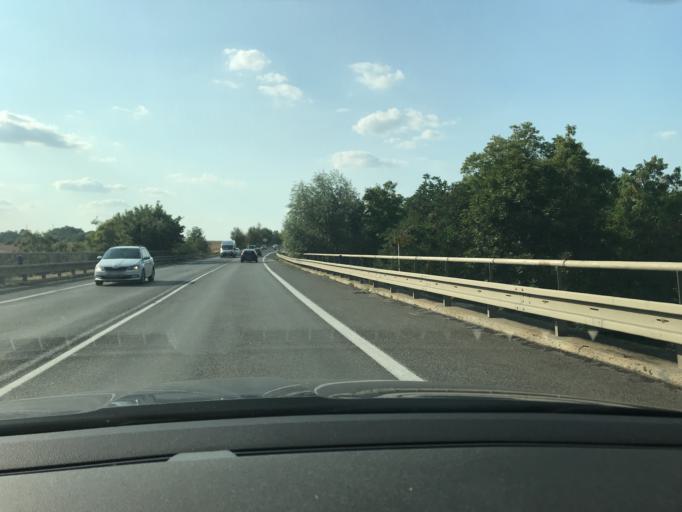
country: CZ
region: Central Bohemia
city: Klobuky
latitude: 50.2600
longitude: 14.0117
